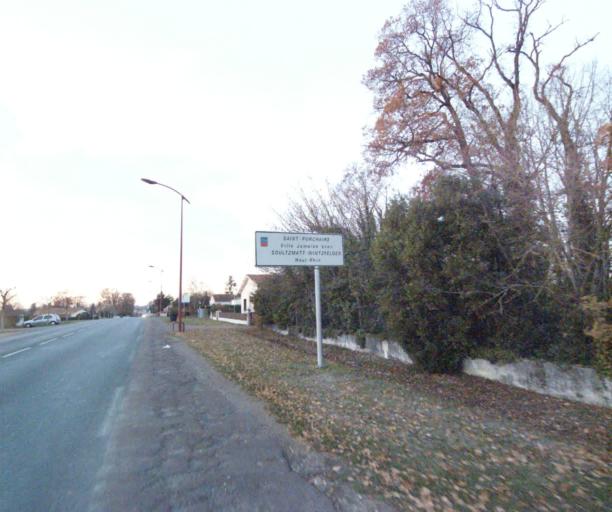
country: FR
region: Poitou-Charentes
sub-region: Departement de la Charente-Maritime
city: Saint-Porchaire
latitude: 45.8172
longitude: -0.7767
